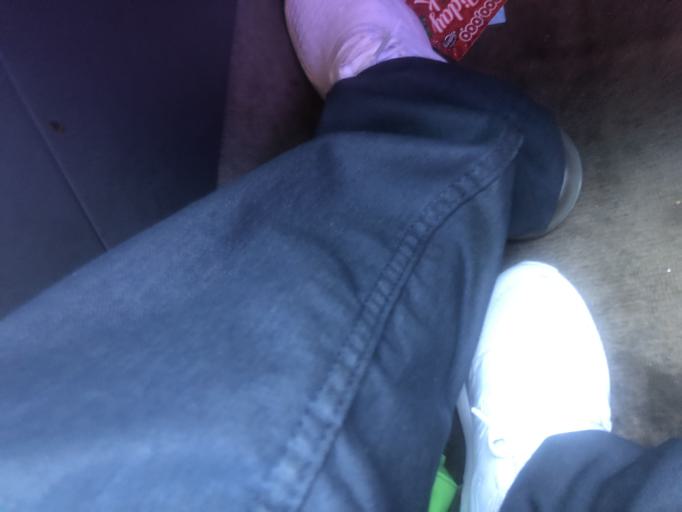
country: US
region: Florida
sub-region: Sumter County
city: Lake Panasoffkee
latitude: 28.7893
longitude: -82.0871
